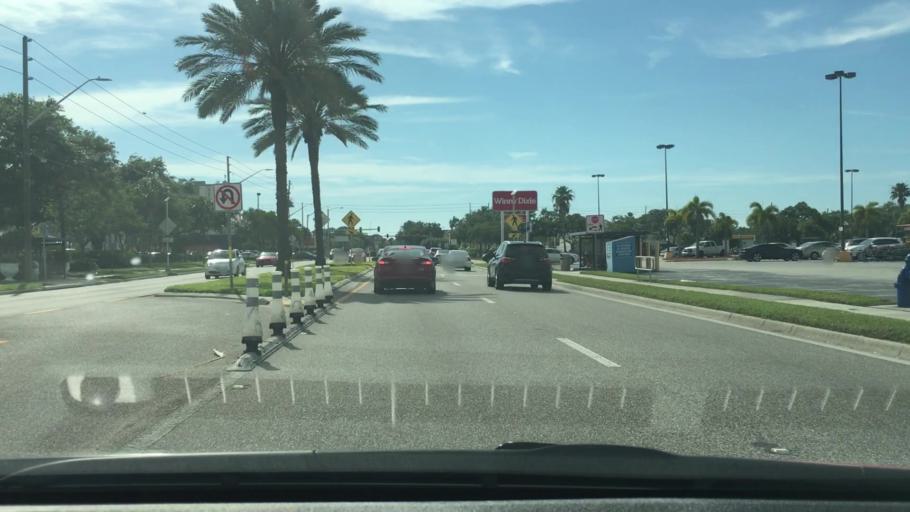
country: US
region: Florida
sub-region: Pinellas County
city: South Pasadena
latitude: 27.7585
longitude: -82.7337
